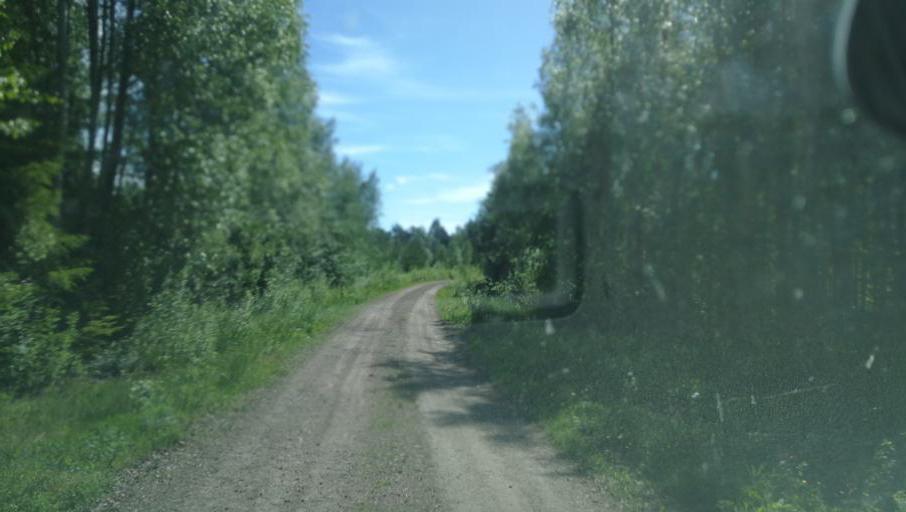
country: SE
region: Dalarna
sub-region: Vansbro Kommun
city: Vansbro
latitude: 60.8280
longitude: 14.1793
